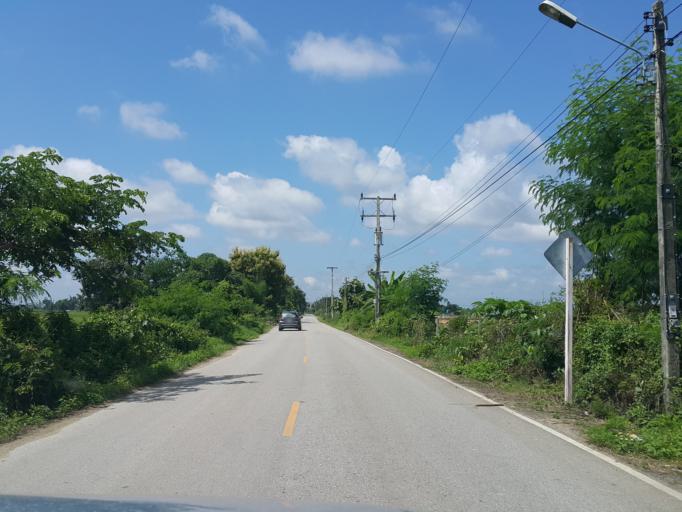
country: TH
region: Chiang Mai
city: San Kamphaeng
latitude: 18.7379
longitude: 99.0975
